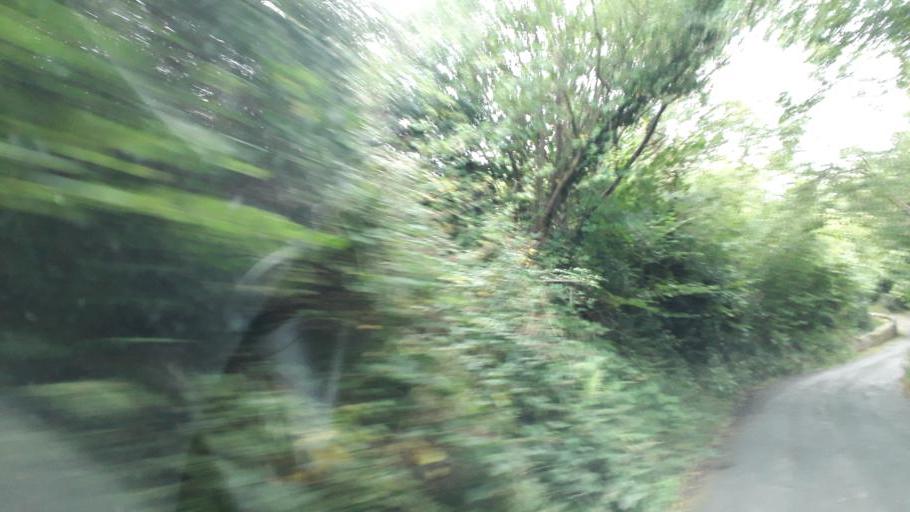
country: IE
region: Leinster
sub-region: Wicklow
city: Enniskerry
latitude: 53.1795
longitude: -6.2048
